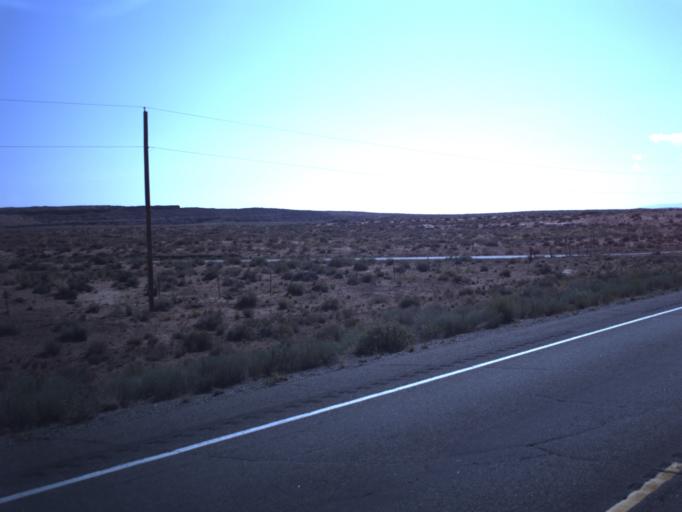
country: US
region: Utah
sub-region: San Juan County
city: Blanding
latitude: 37.1408
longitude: -109.5587
